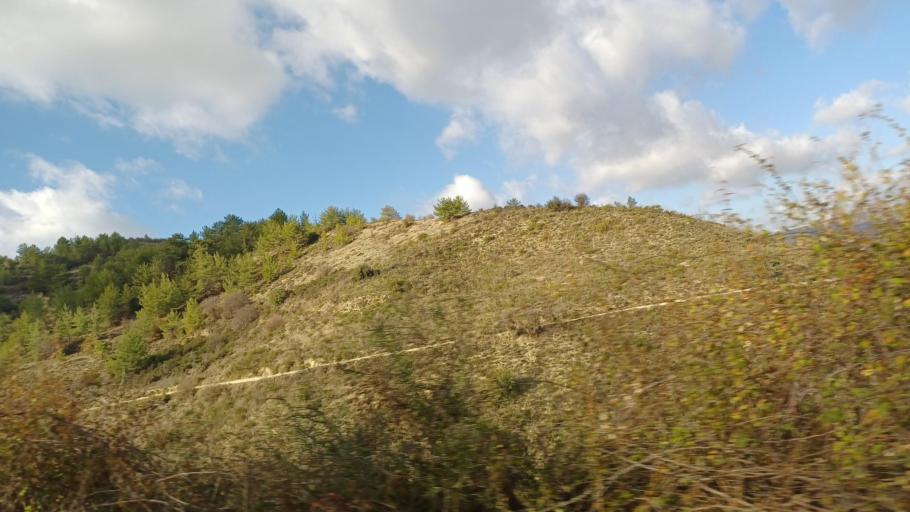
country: CY
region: Limassol
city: Pachna
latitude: 34.8539
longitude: 32.6896
